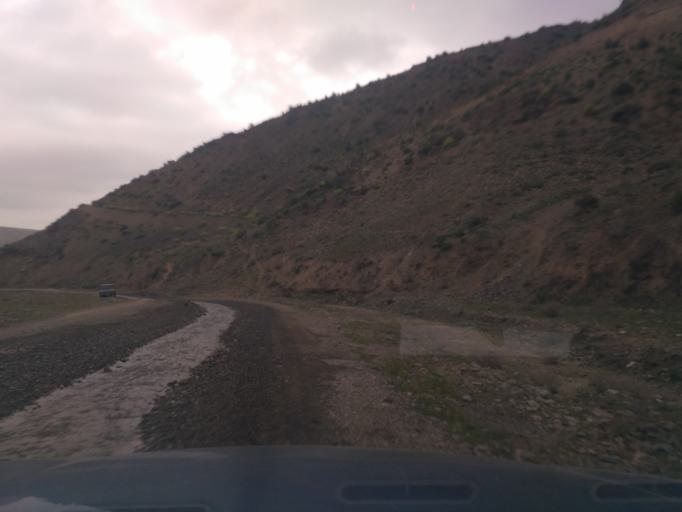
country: UZ
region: Jizzax
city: Zomin
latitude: 39.8583
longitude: 68.3878
